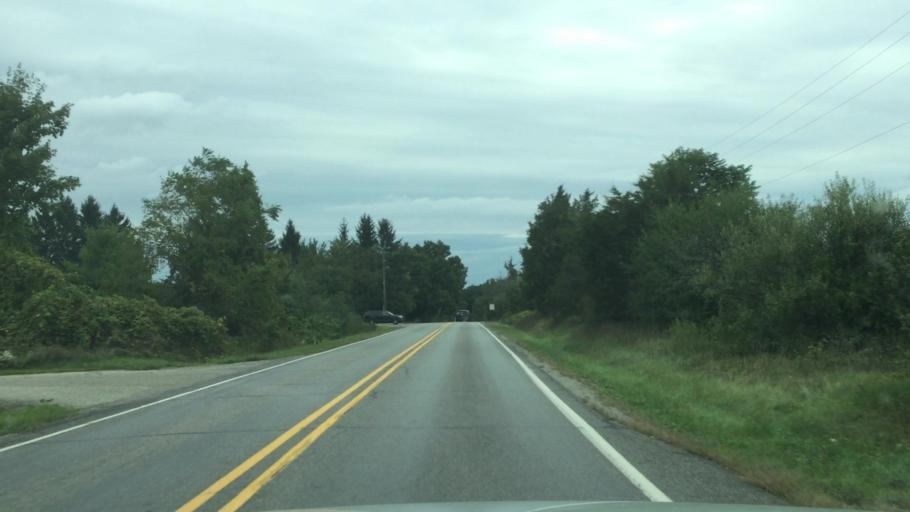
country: US
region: Michigan
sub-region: Livingston County
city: Whitmore Lake
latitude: 42.4667
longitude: -83.7665
